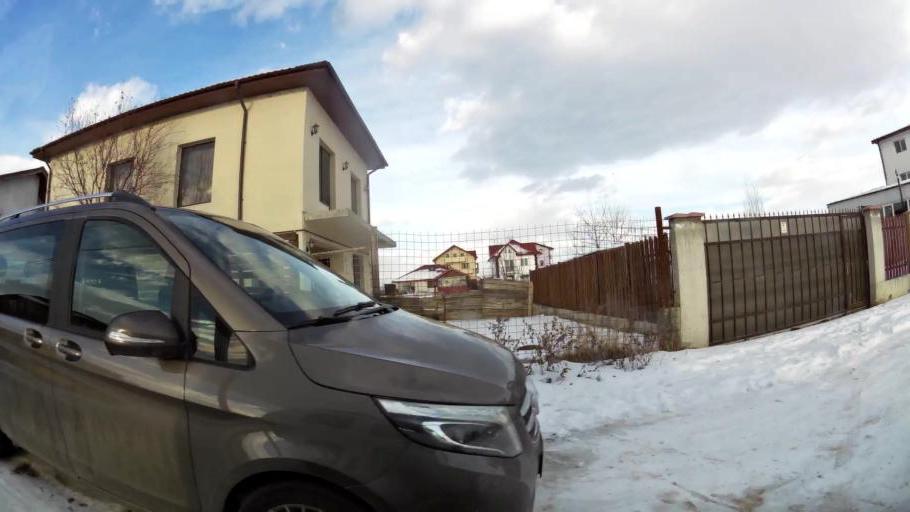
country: RO
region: Ilfov
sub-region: Comuna Fundeni-Dobroesti
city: Fundeni
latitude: 44.4646
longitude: 26.1789
